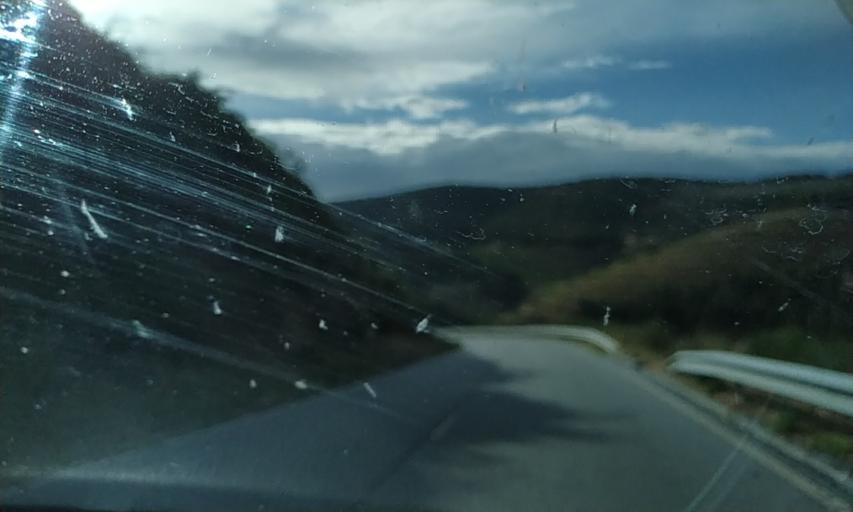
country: PT
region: Viseu
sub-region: Sao Joao da Pesqueira
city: Sao Joao da Pesqueira
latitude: 41.1074
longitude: -7.4647
